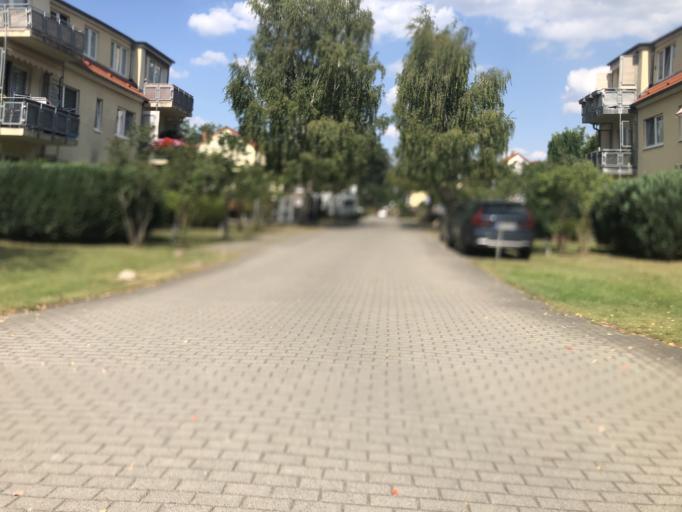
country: DE
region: Brandenburg
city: Mullrose
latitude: 52.2311
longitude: 14.4121
